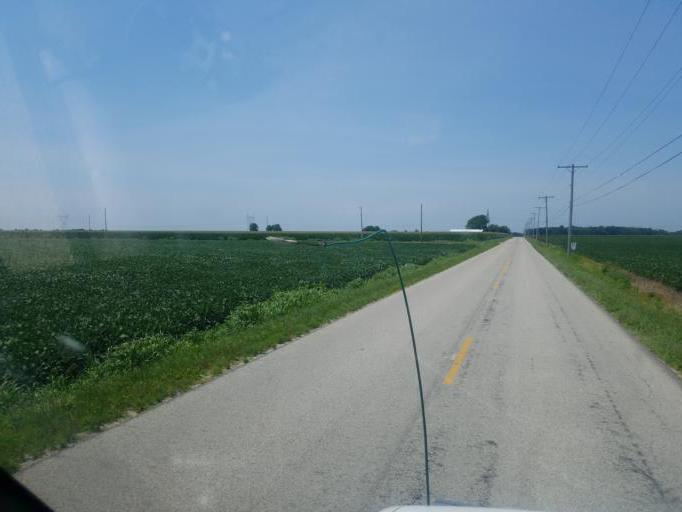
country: US
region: Ohio
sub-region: Shelby County
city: Sidney
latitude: 40.3043
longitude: -84.0781
